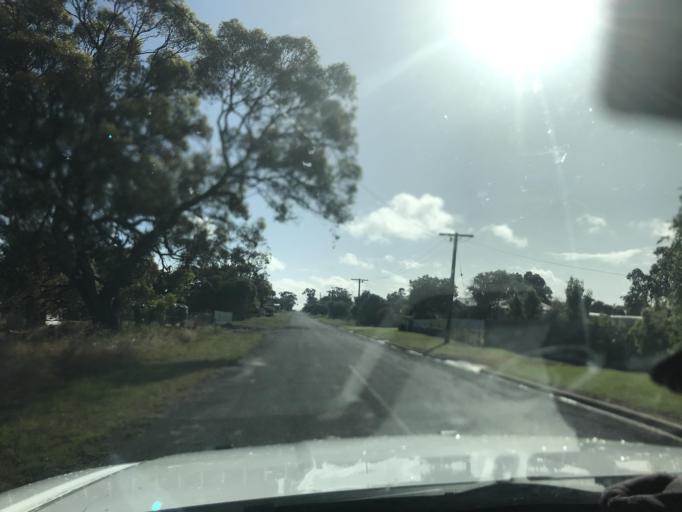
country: AU
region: Victoria
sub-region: Horsham
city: Horsham
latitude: -36.7204
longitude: 141.4706
